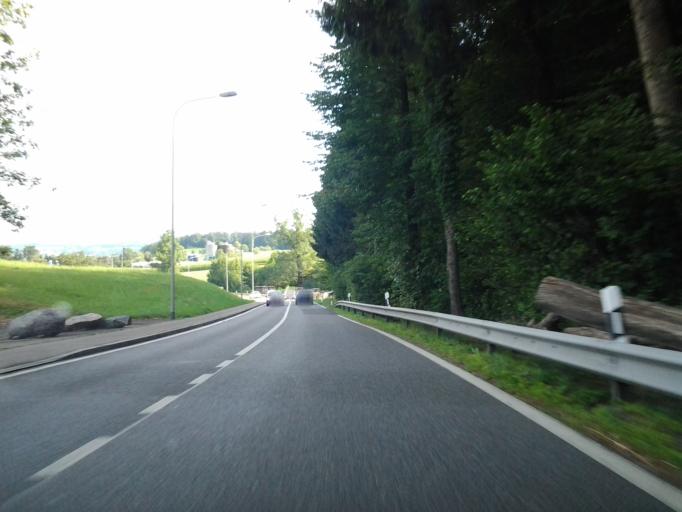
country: CH
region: Zurich
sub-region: Bezirk Horgen
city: Au / Unter-Dorf
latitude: 47.2265
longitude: 8.6265
